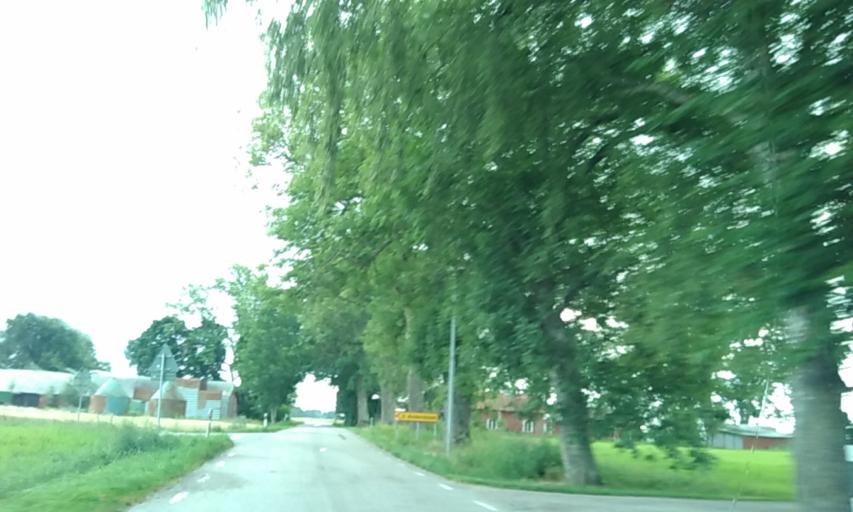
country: SE
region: Vaestra Goetaland
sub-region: Grastorps Kommun
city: Graestorp
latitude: 58.4488
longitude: 12.7769
